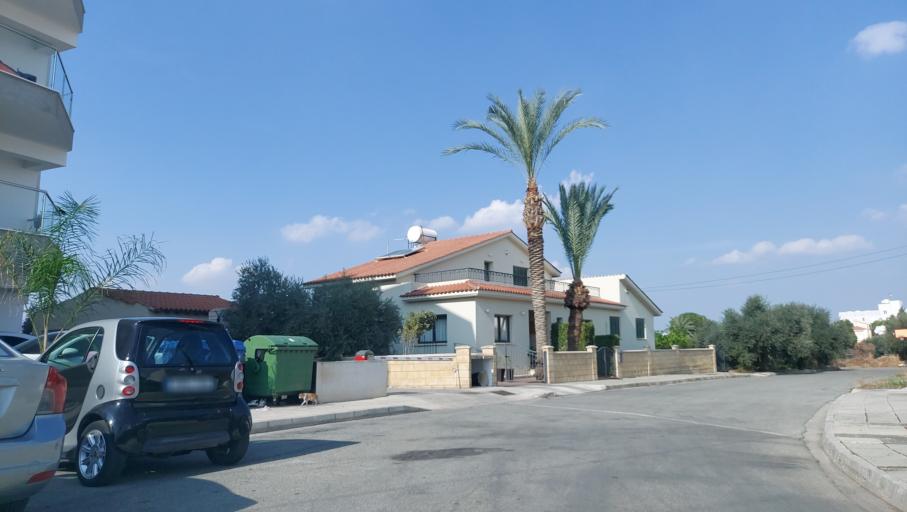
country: CY
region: Lefkosia
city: Kato Deftera
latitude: 35.1071
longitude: 33.3057
